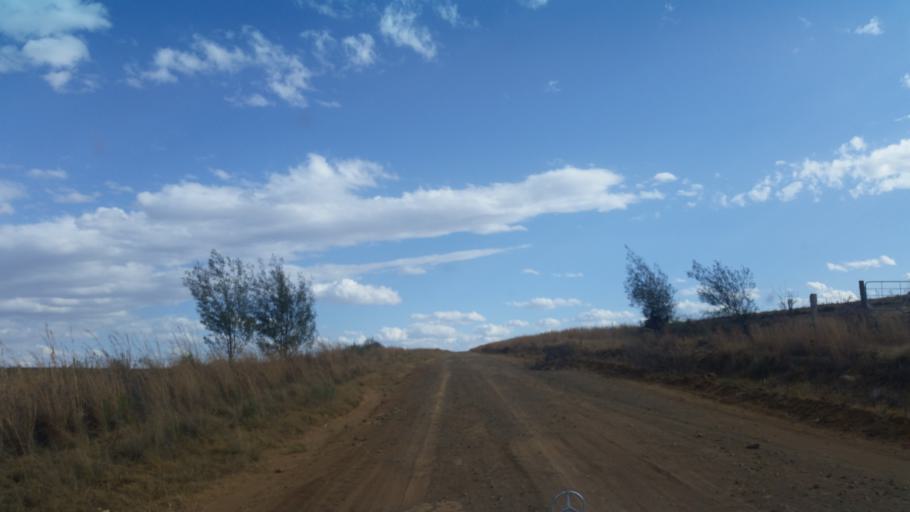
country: ZA
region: Orange Free State
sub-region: Thabo Mofutsanyana District Municipality
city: Phuthaditjhaba
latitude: -28.3550
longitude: 28.6030
